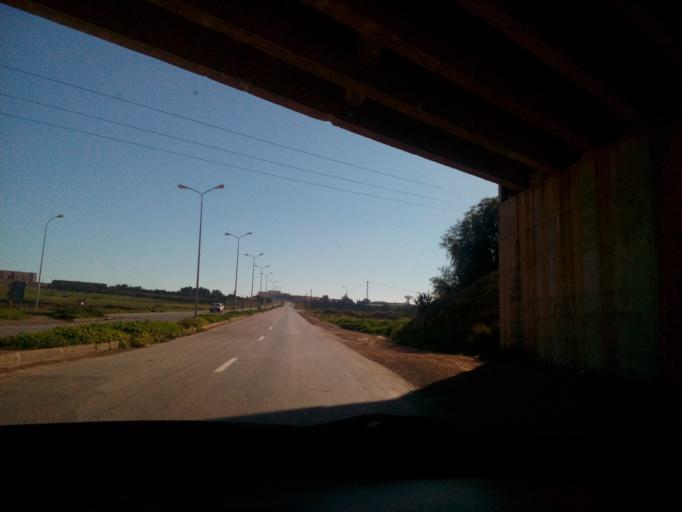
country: DZ
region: Relizane
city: Relizane
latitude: 35.7166
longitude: 0.5077
